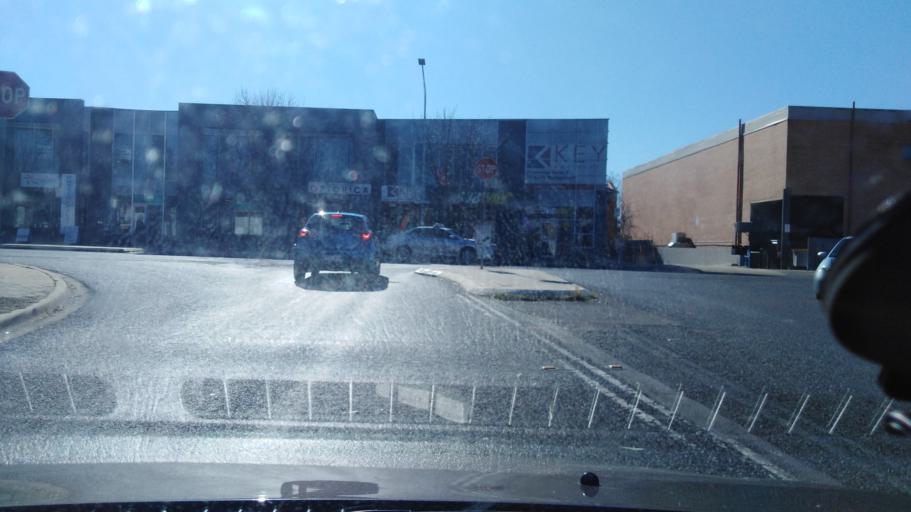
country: AU
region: Australian Capital Territory
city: Forrest
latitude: -35.3401
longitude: 149.0523
